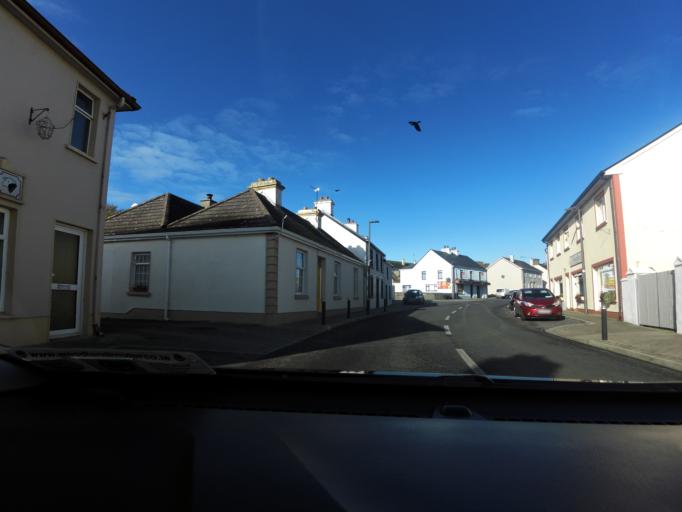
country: IE
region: Connaught
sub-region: Maigh Eo
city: Ballinrobe
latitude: 53.5202
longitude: -9.0882
